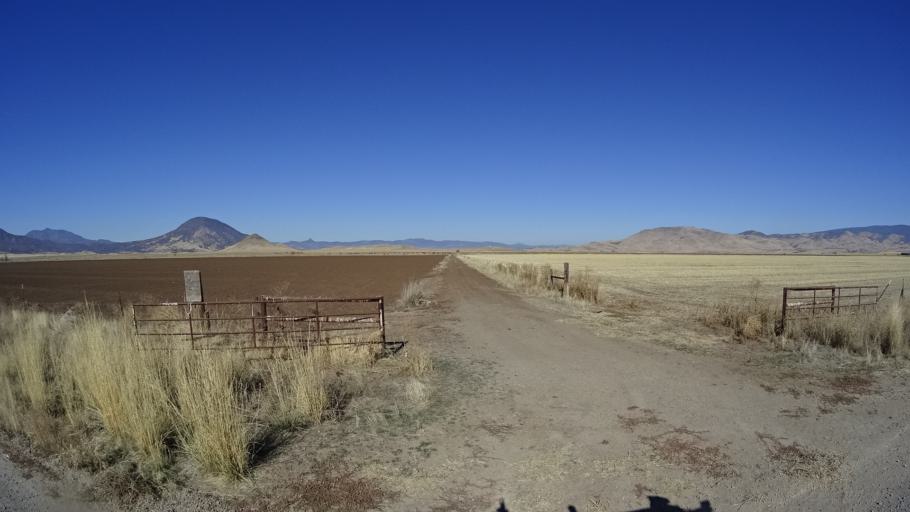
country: US
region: California
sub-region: Siskiyou County
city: Montague
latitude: 41.7865
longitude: -122.4509
